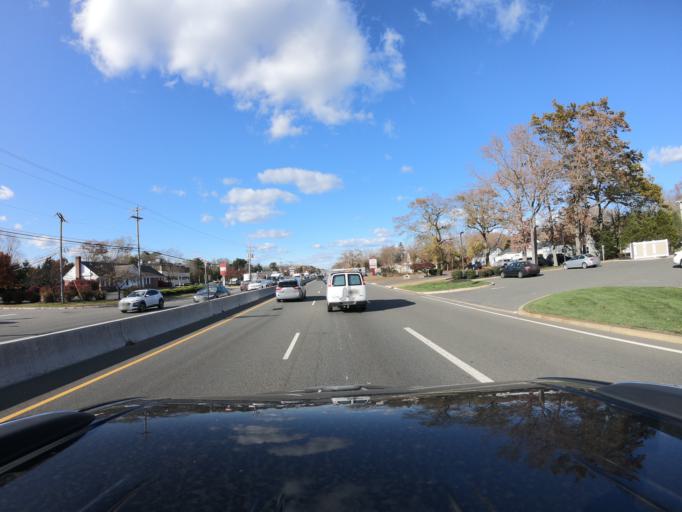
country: US
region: New Jersey
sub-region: Ocean County
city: Lakewood
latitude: 40.1567
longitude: -74.2305
